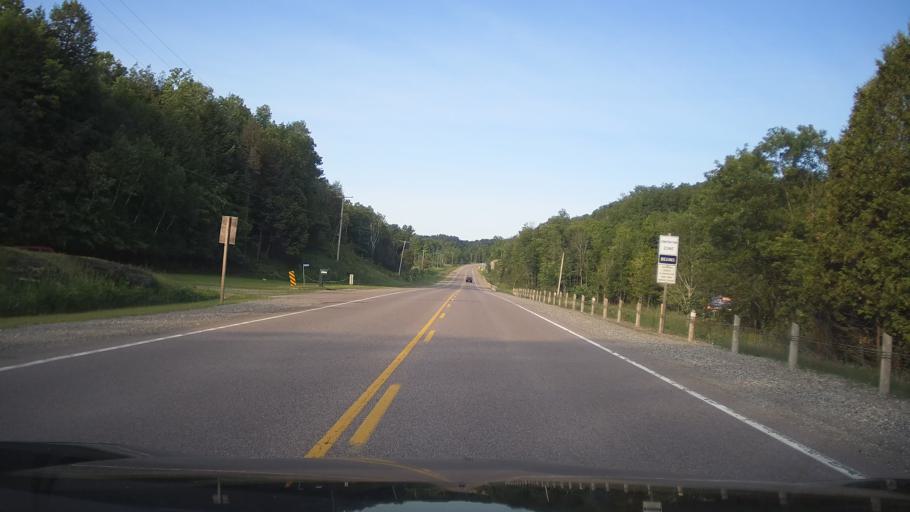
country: CA
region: Ontario
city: Skatepark
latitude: 44.7458
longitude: -76.9204
